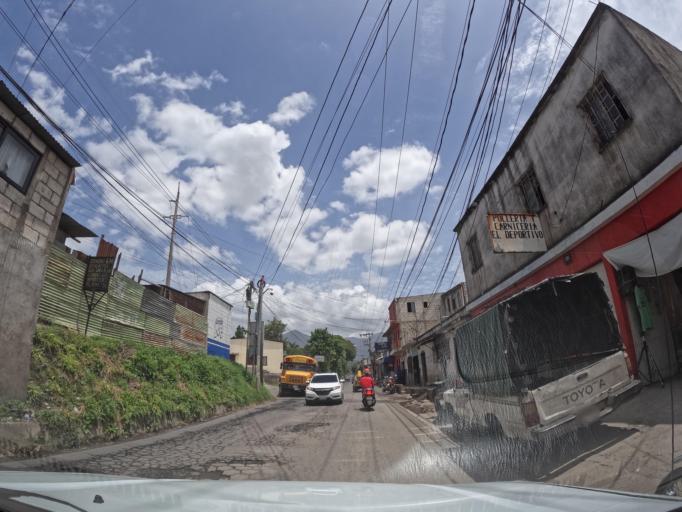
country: GT
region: Guatemala
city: Amatitlan
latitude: 14.4773
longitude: -90.6104
